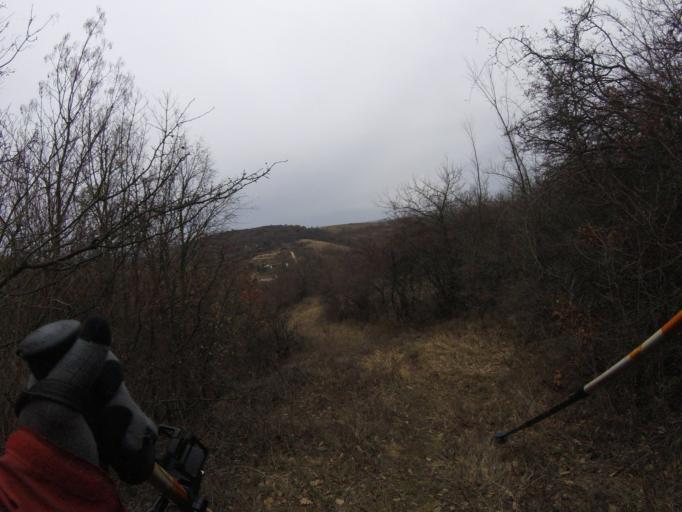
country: HU
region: Komarom-Esztergom
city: Kesztolc
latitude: 47.7157
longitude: 18.8133
